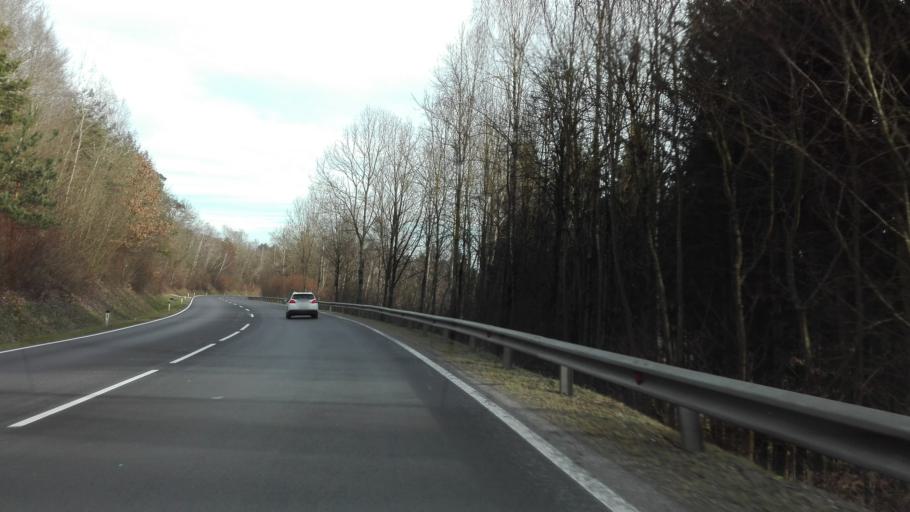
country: AT
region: Upper Austria
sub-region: Politischer Bezirk Urfahr-Umgebung
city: Herzogsdorf
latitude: 48.4048
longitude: 14.0691
